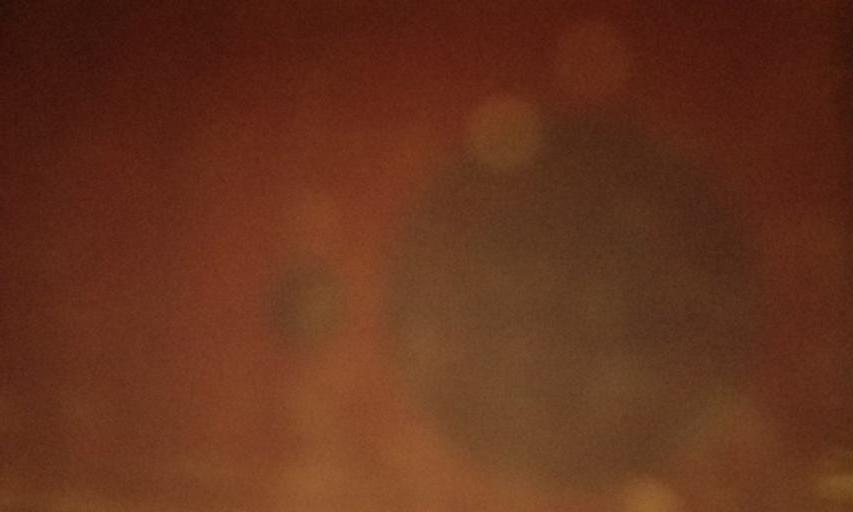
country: JP
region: Hiroshima
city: Onomichi
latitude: 34.4245
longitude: 133.1738
